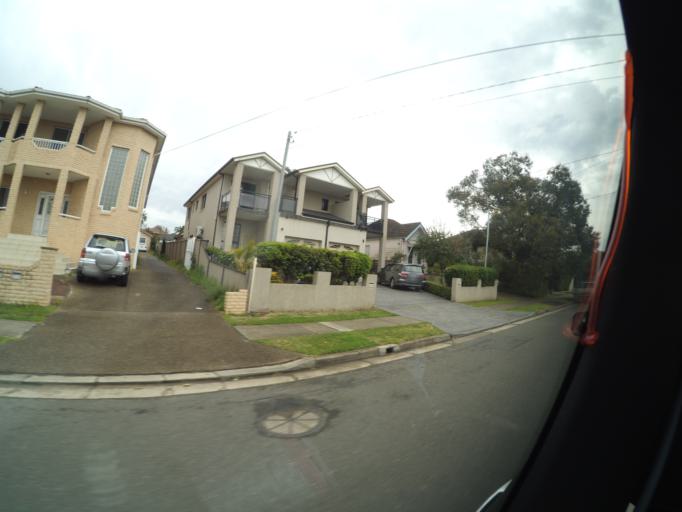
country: AU
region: New South Wales
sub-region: Bankstown
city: Bankstown
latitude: -33.9196
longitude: 151.0260
